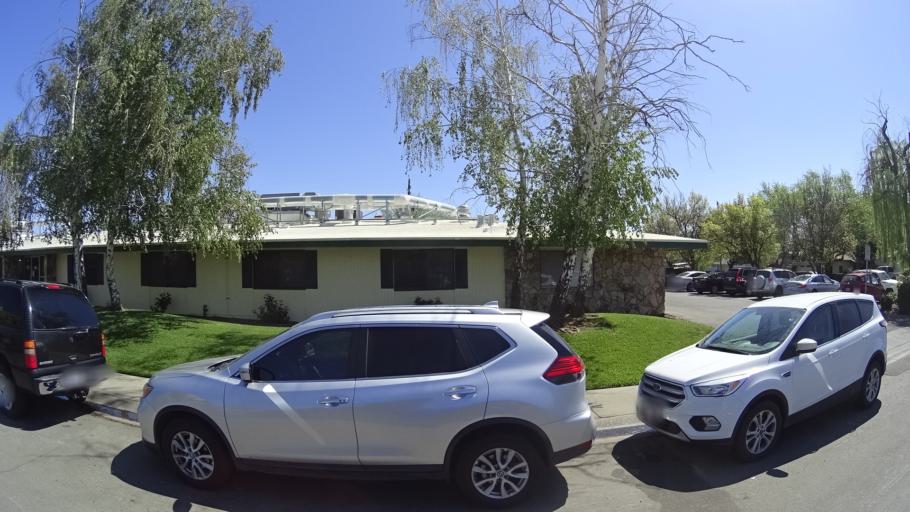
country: US
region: California
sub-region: Glenn County
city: Willows
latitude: 39.5234
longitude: -122.2061
